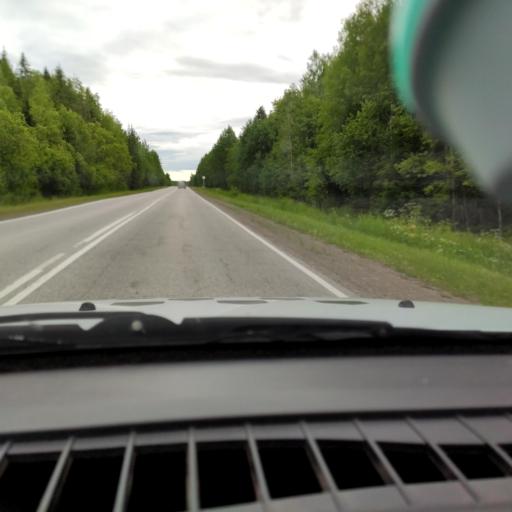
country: RU
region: Perm
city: Lys'va
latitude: 58.1261
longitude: 57.7219
